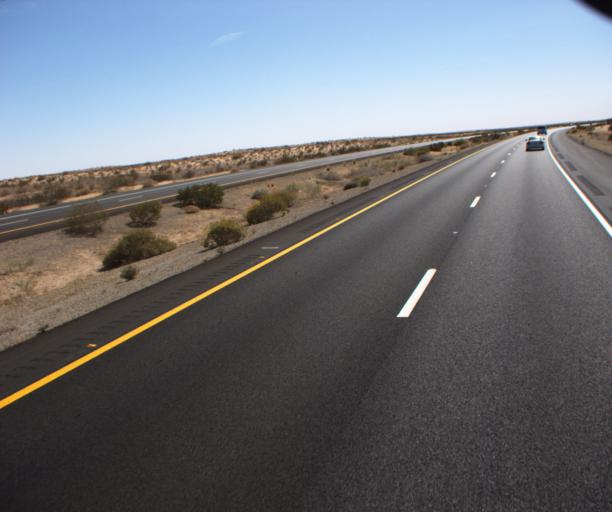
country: US
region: Arizona
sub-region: Yuma County
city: Fortuna Foothills
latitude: 32.6143
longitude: -114.5234
